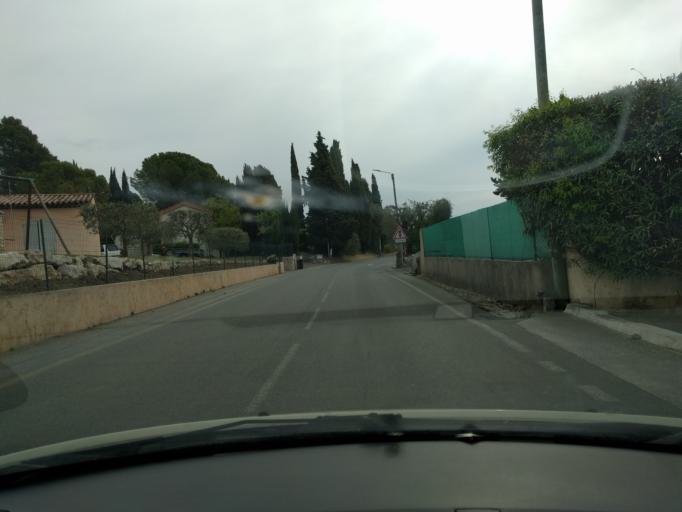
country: FR
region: Provence-Alpes-Cote d'Azur
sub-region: Departement des Alpes-Maritimes
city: La Roquette-sur-Siagne
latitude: 43.5808
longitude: 6.9538
